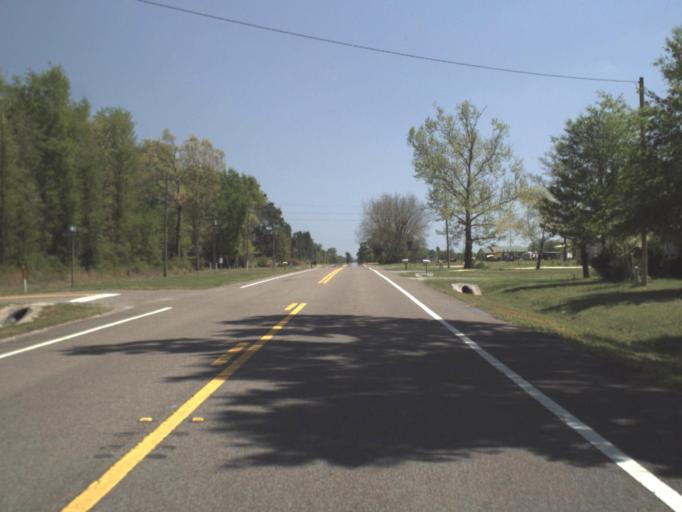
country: US
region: Alabama
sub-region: Escambia County
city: East Brewton
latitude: 30.9383
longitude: -87.0640
